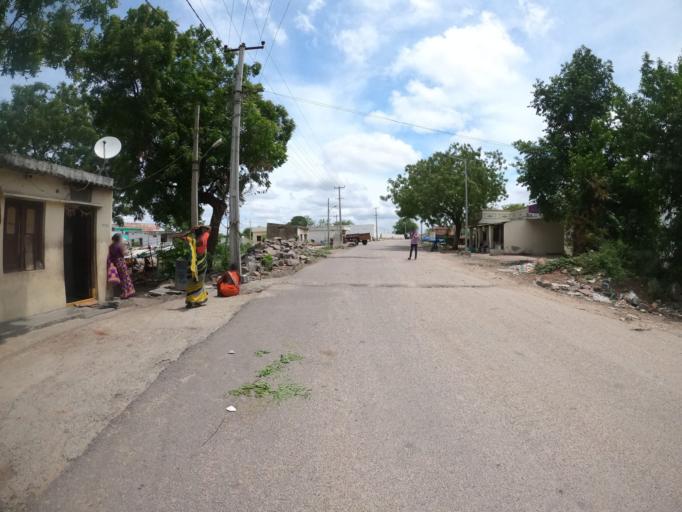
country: IN
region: Telangana
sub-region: Hyderabad
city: Hyderabad
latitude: 17.2982
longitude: 78.3785
